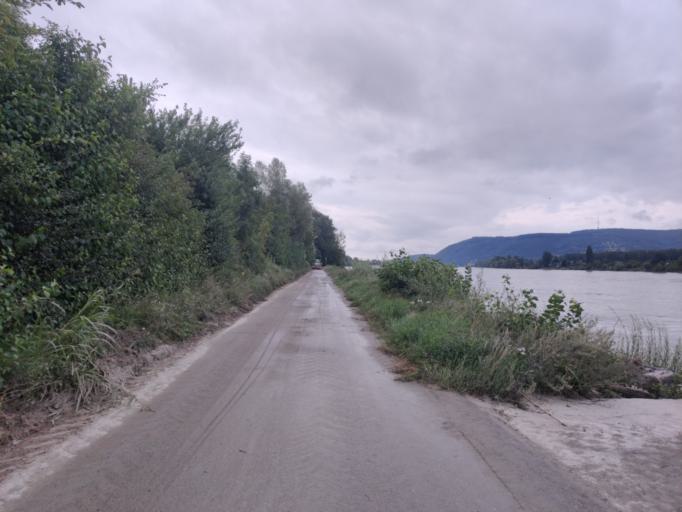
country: AT
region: Lower Austria
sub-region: Politischer Bezirk Korneuburg
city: Bisamberg
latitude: 48.3219
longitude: 16.3380
